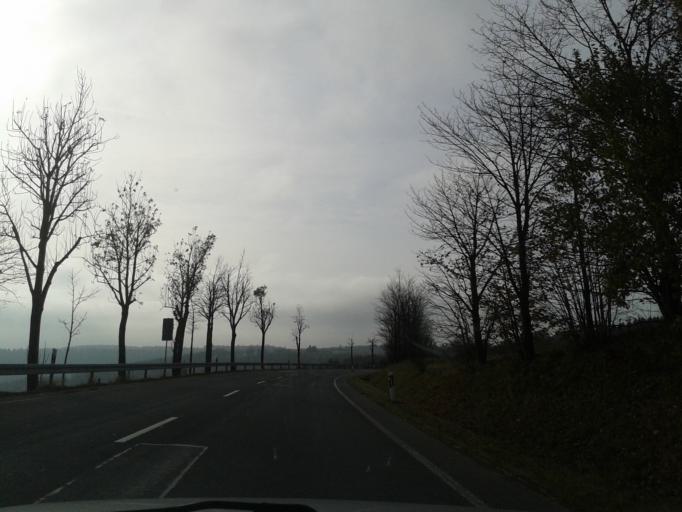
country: DE
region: North Rhine-Westphalia
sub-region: Regierungsbezirk Arnsberg
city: Winterberg
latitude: 51.1485
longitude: 8.4596
